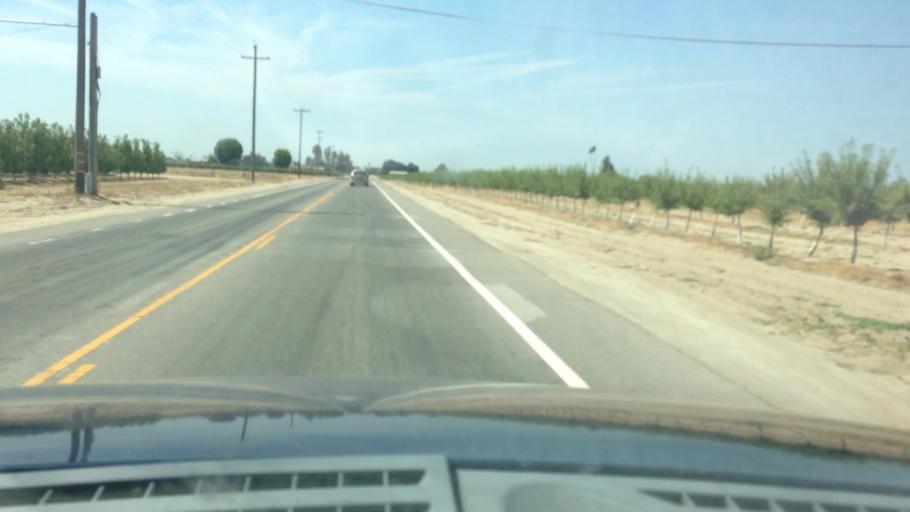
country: US
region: California
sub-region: Fresno County
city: Kingsburg
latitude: 36.5612
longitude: -119.5567
